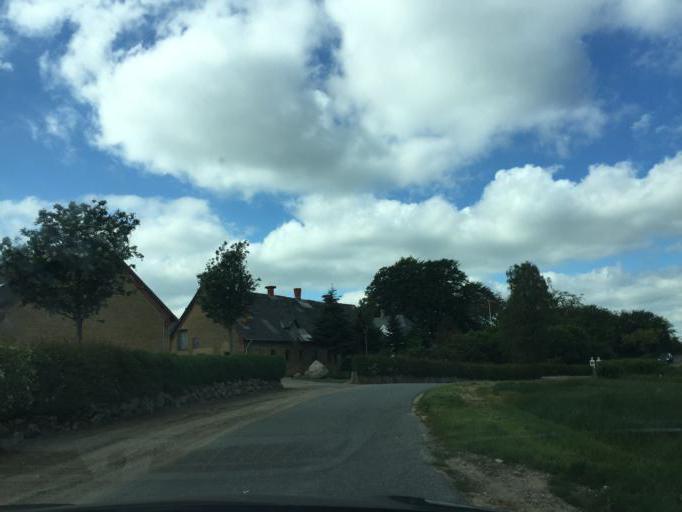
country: DK
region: South Denmark
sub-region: Assens Kommune
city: Tommerup
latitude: 55.3412
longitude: 10.2003
